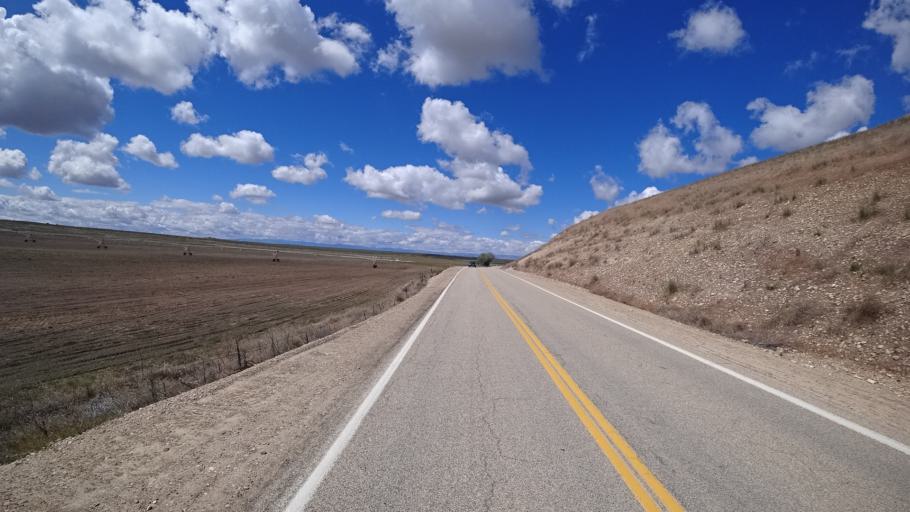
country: US
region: Idaho
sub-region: Ada County
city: Boise
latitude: 43.4868
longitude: -116.2387
